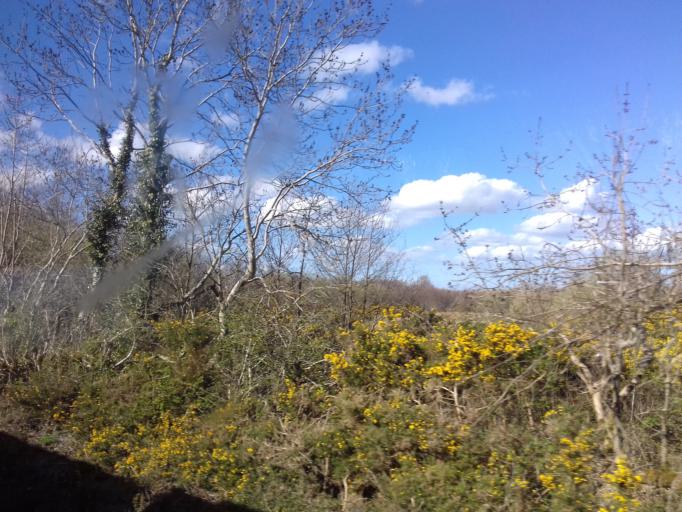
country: IE
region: Munster
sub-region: County Cork
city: Kanturk
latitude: 52.1267
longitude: -8.8214
